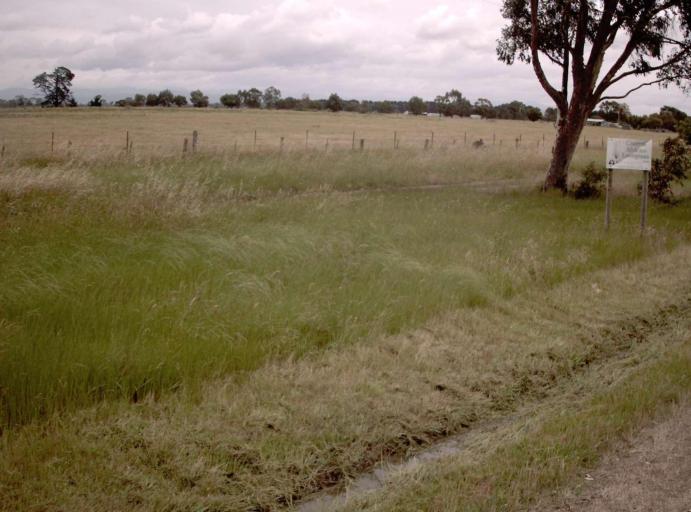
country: AU
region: Victoria
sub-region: Wellington
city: Sale
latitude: -37.9536
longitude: 147.0861
